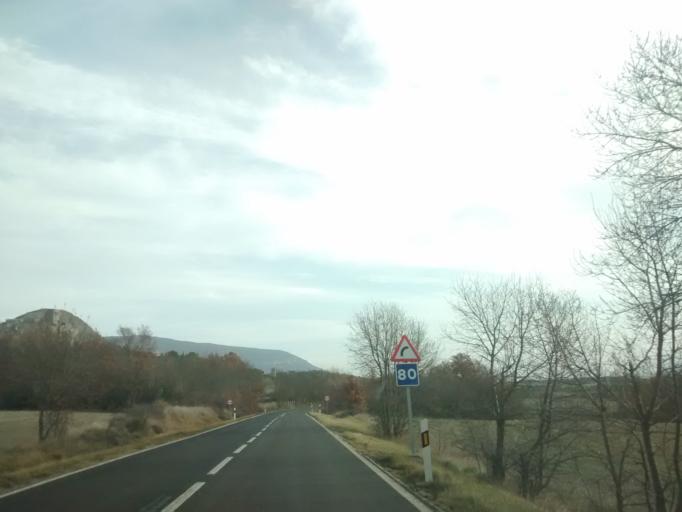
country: ES
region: Aragon
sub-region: Provincia de Zaragoza
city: Siguees
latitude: 42.6158
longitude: -1.0647
